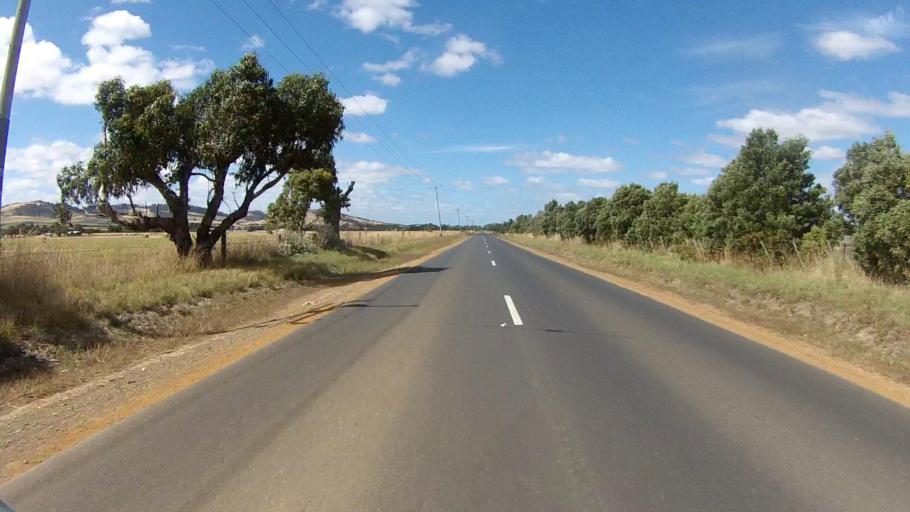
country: AU
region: Tasmania
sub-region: Clarence
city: Cambridge
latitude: -42.7164
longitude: 147.4319
